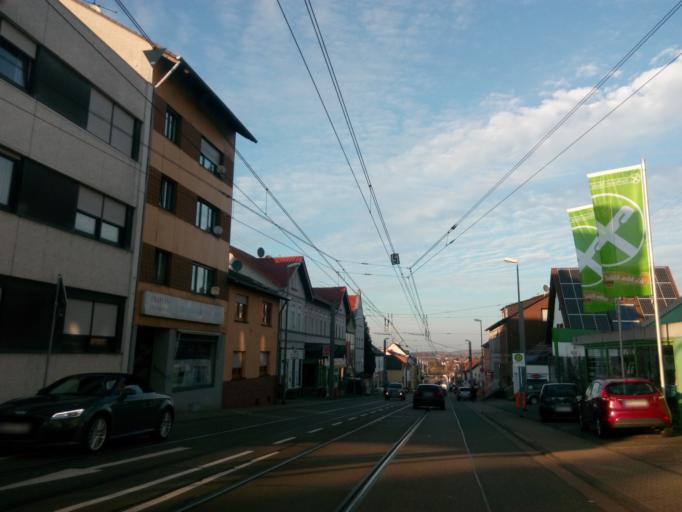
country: DE
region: Saarland
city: Riegelsberg
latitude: 49.3024
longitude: 6.9439
